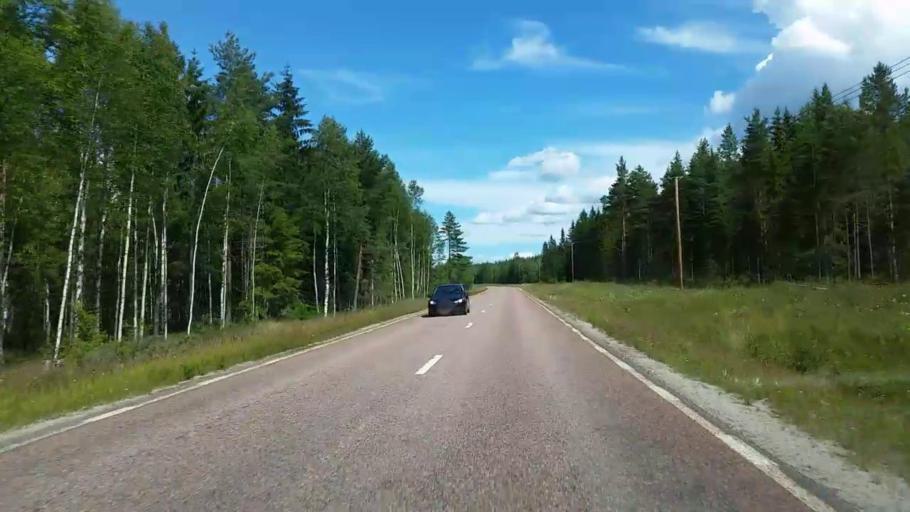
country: SE
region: Dalarna
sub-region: Rattviks Kommun
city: Raettvik
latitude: 61.1965
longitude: 15.3367
